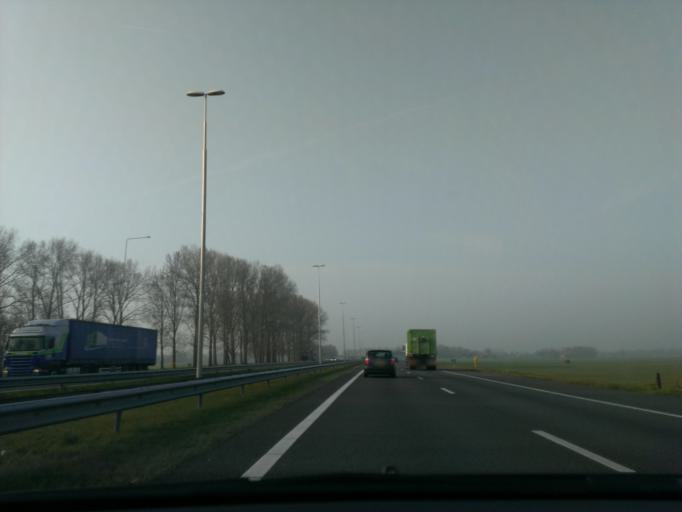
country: NL
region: Gelderland
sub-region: Gemeente Epe
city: Vaassen
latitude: 52.2756
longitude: 6.0059
